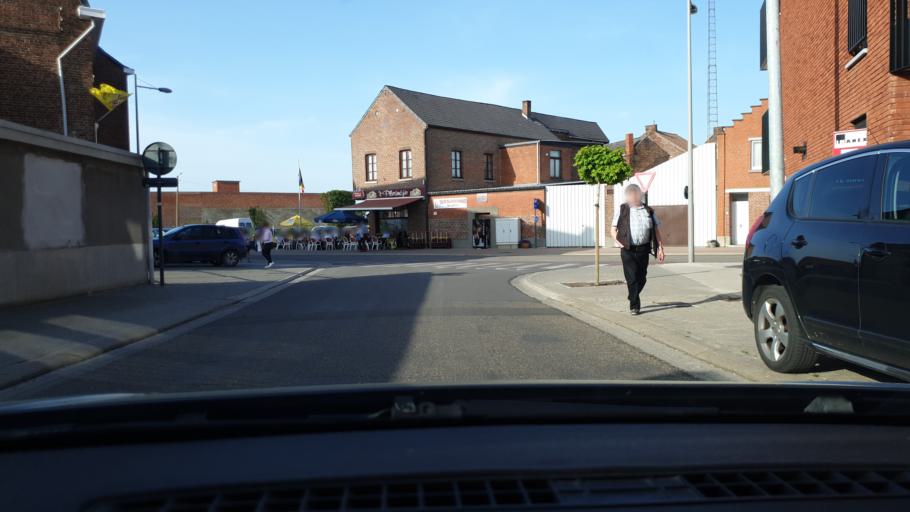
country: BE
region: Flanders
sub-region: Provincie Limburg
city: Borgloon
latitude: 50.8097
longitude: 5.3422
